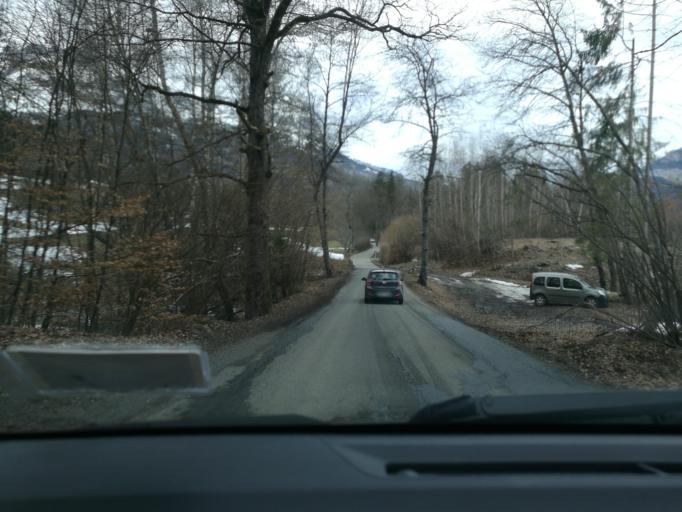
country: FR
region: Rhone-Alpes
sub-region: Departement de la Haute-Savoie
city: Domancy
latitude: 45.9153
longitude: 6.6306
